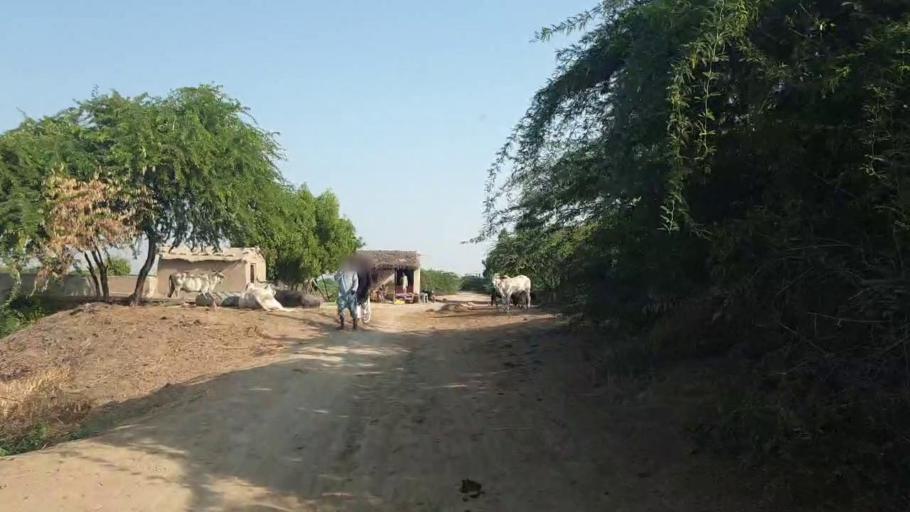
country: PK
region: Sindh
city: Badin
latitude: 24.4683
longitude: 68.7399
